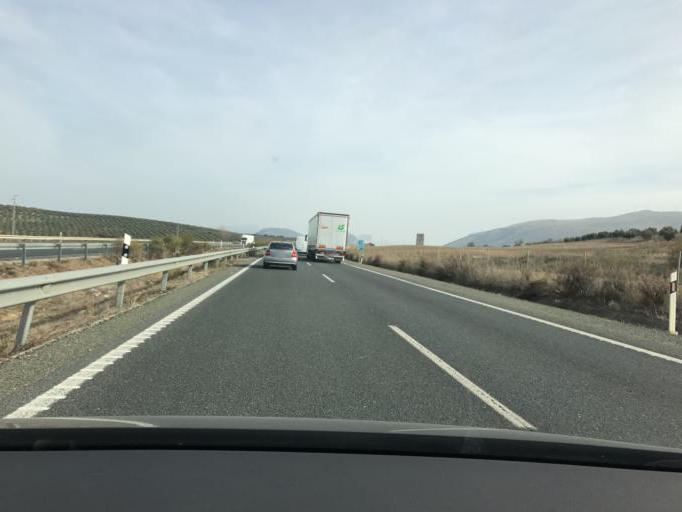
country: ES
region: Andalusia
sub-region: Provincia de Malaga
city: Villanueva de Tapia
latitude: 37.1446
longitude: -4.2584
